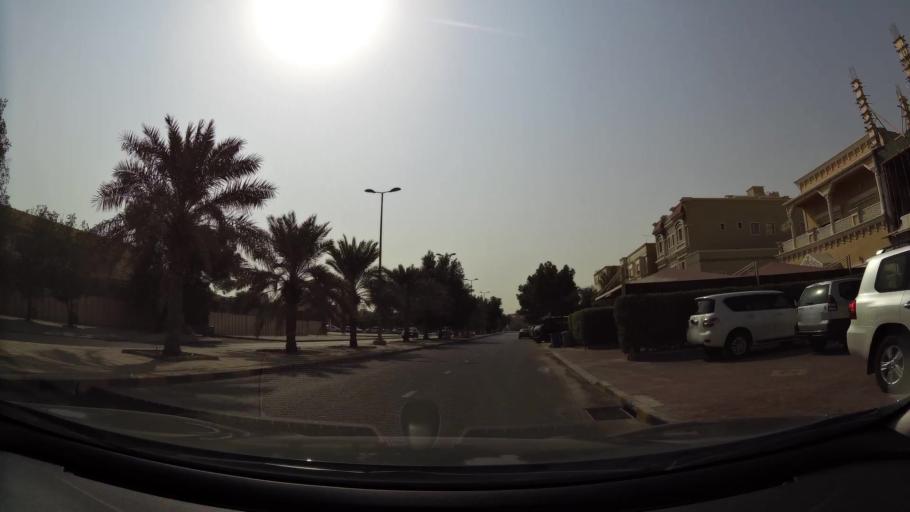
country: KW
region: Al Asimah
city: Ar Rabiyah
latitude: 29.2916
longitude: 47.8933
